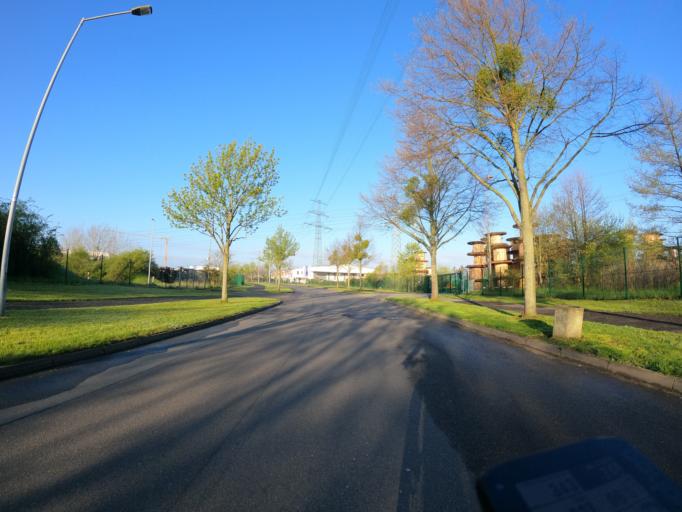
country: DE
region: Brandenburg
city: Neuenhagen
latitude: 52.5378
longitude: 13.7113
